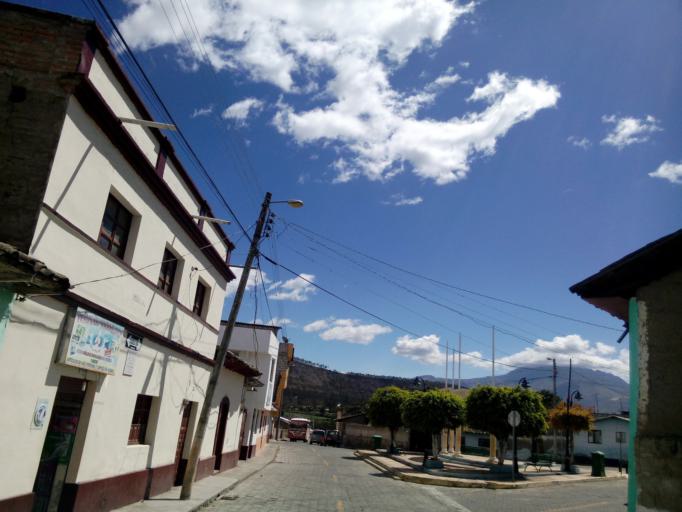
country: EC
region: Imbabura
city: Atuntaqui
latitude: 0.4168
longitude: -78.1925
